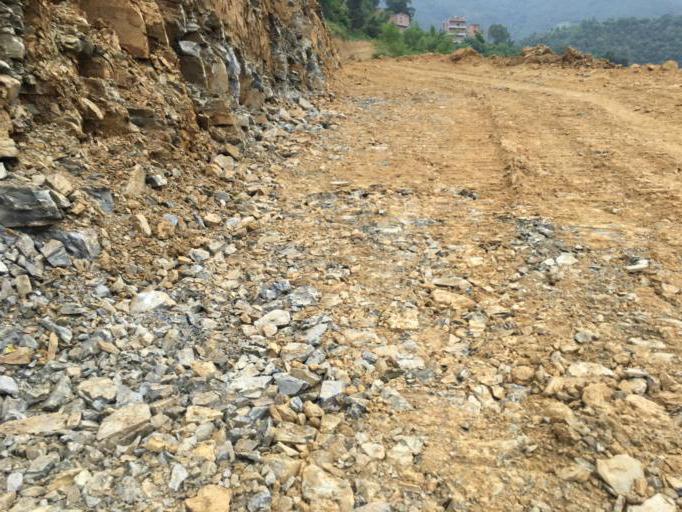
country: CN
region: Guangxi Zhuangzu Zizhiqu
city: Tongle
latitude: 25.1228
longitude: 106.4228
